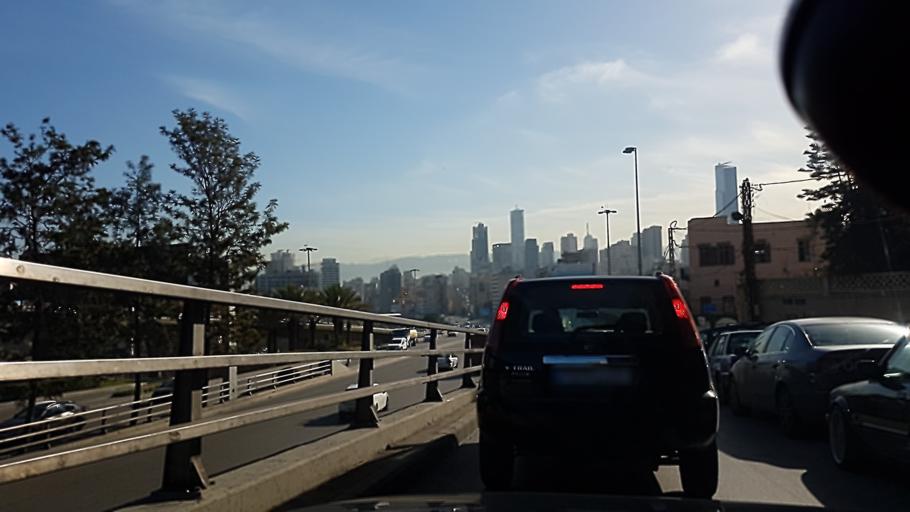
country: LB
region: Beyrouth
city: Beirut
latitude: 33.8939
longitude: 35.5000
